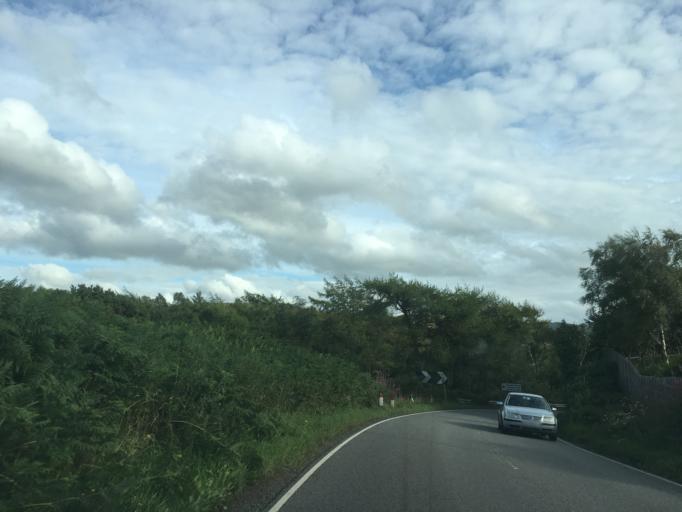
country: GB
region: Scotland
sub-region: Argyll and Bute
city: Oban
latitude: 56.3893
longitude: -5.4588
